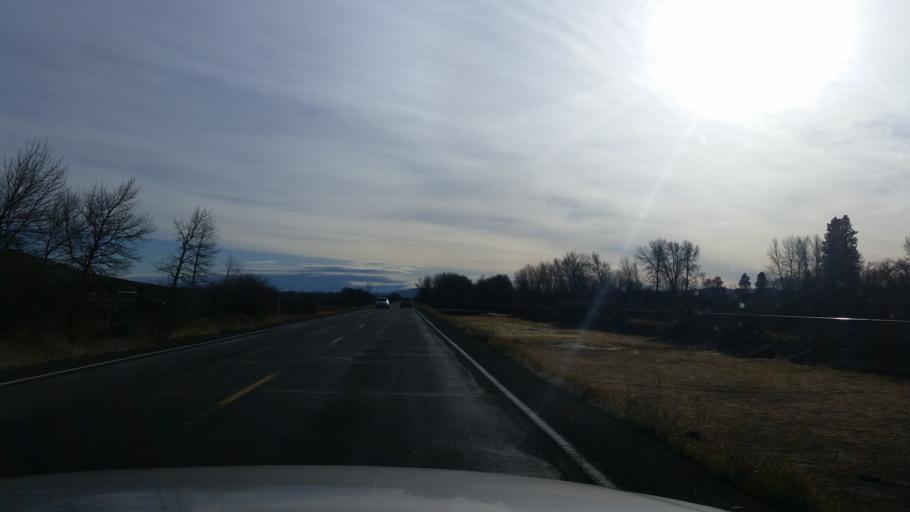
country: US
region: Washington
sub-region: Kittitas County
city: Ellensburg
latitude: 47.0516
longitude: -120.6358
